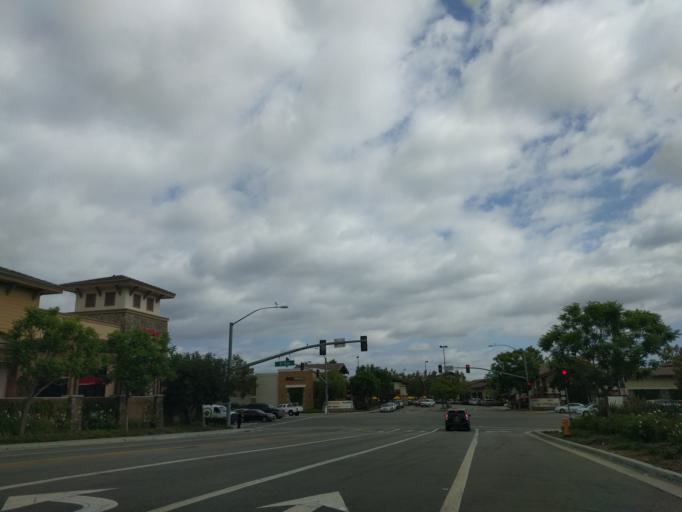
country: US
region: California
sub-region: Orange County
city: Laguna Hills
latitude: 33.6191
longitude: -117.7034
